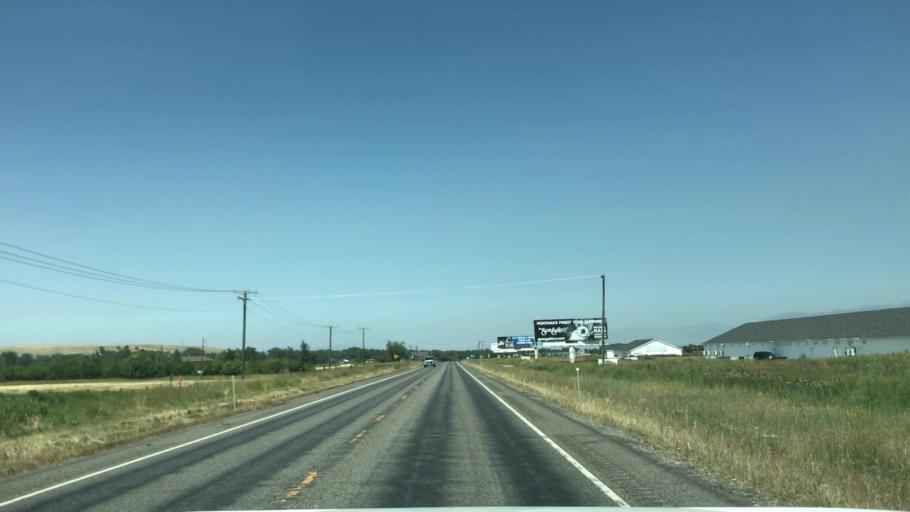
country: US
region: Montana
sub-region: Gallatin County
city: Four Corners
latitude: 45.6336
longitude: -111.1969
